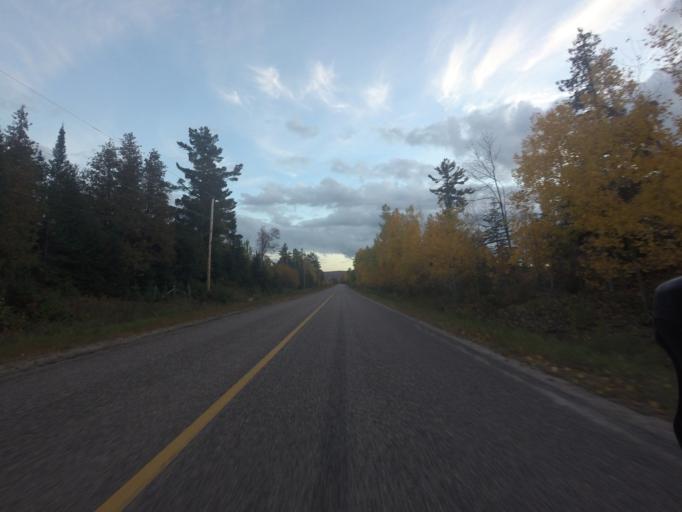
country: CA
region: Ontario
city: Renfrew
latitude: 45.3845
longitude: -76.9564
